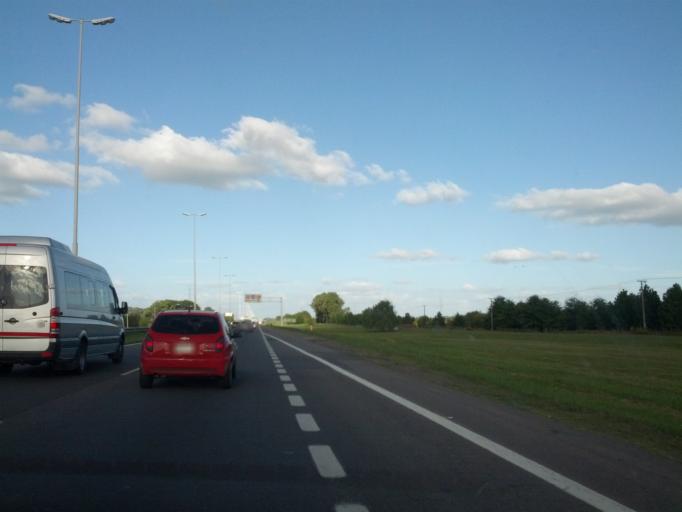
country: AR
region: Buenos Aires
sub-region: Partido de Lujan
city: Lujan
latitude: -34.5696
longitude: -59.0566
